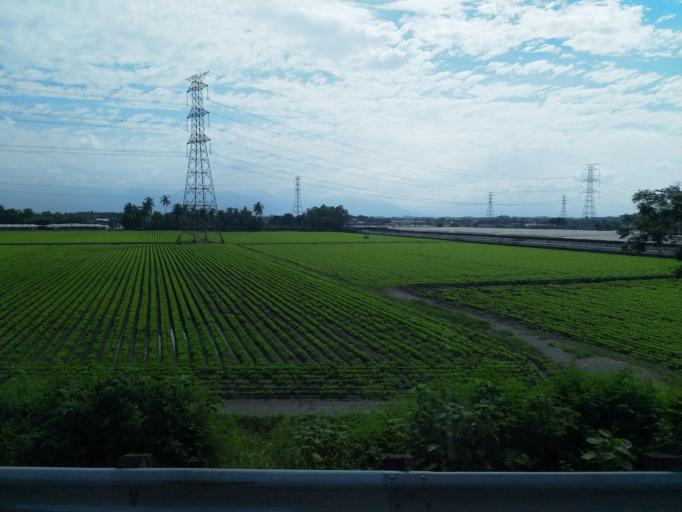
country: TW
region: Taiwan
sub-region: Pingtung
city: Pingtung
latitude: 22.8293
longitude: 120.4900
